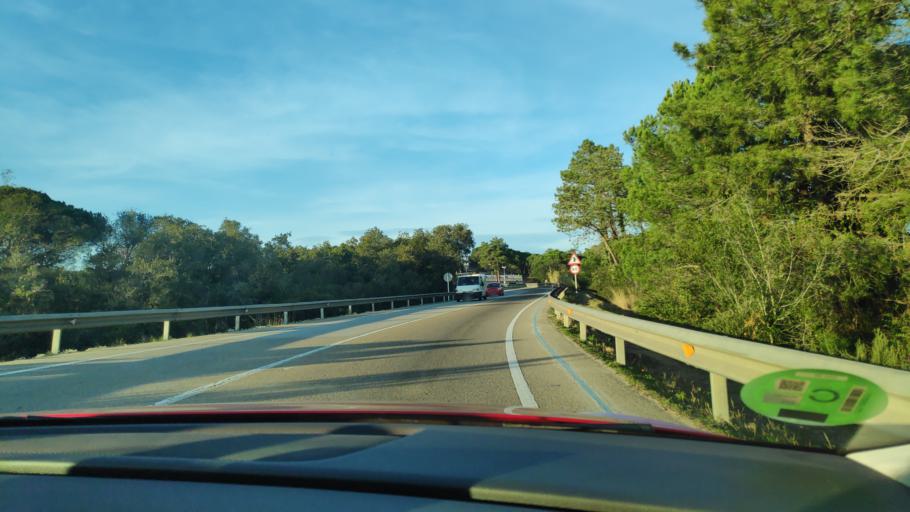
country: ES
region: Catalonia
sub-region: Provincia de Girona
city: Lloret de Mar
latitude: 41.7213
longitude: 2.8251
